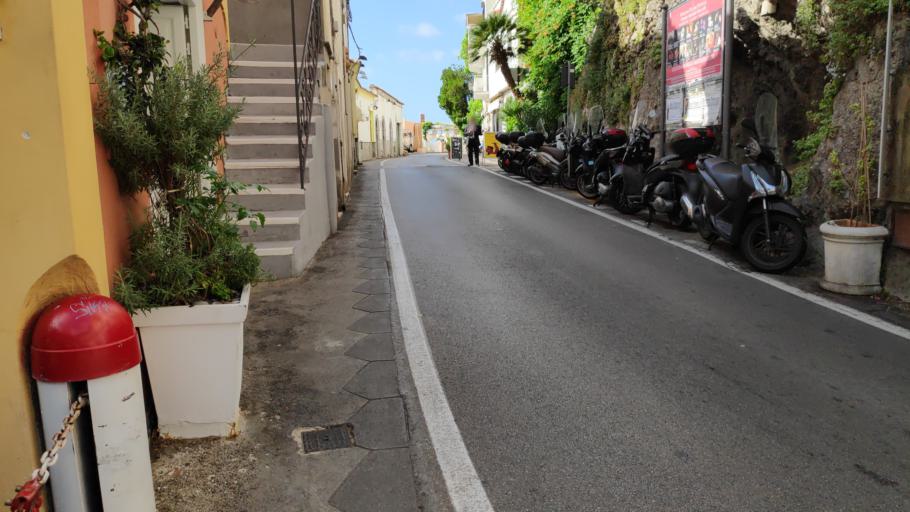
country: IT
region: Campania
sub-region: Provincia di Salerno
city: Positano
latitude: 40.6285
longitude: 14.4852
